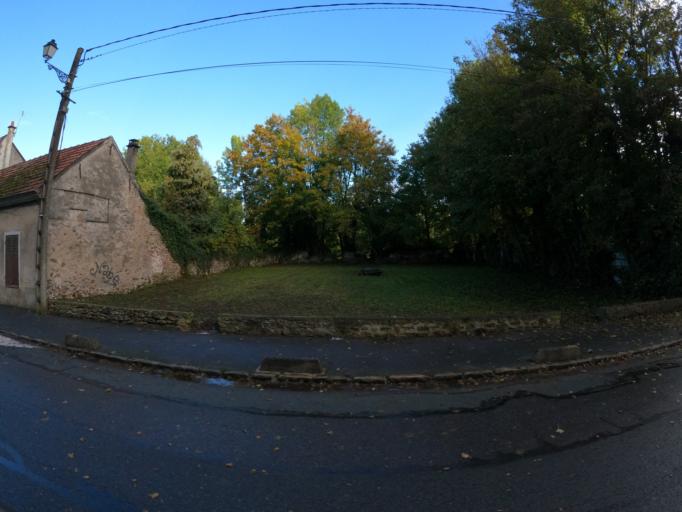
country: FR
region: Ile-de-France
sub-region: Departement de Seine-et-Marne
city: Chanteloup-en-Brie
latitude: 48.8379
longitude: 2.7551
